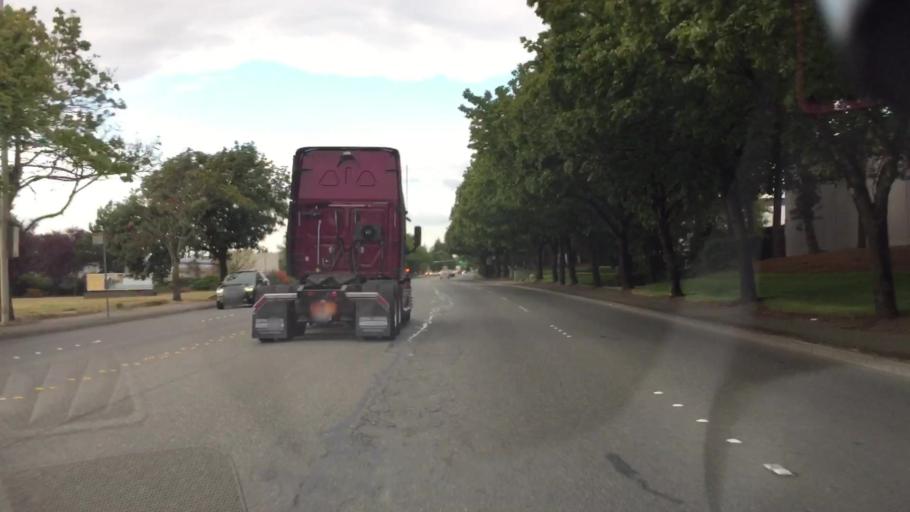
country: US
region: Washington
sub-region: King County
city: Kent
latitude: 47.4221
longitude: -122.2280
